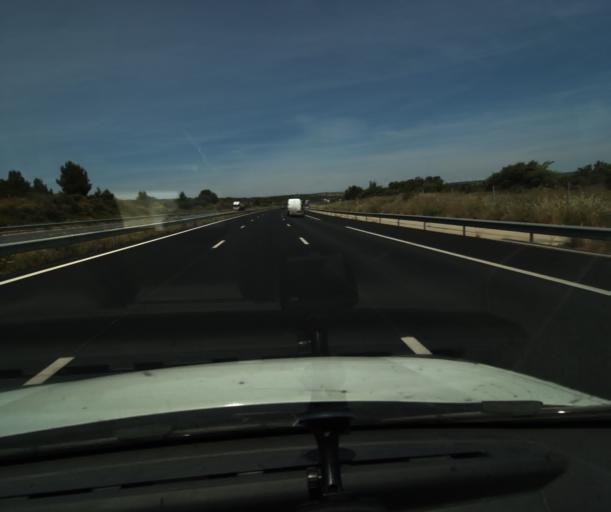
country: FR
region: Languedoc-Roussillon
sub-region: Departement de l'Aude
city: Sigean
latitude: 42.9663
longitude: 2.9688
